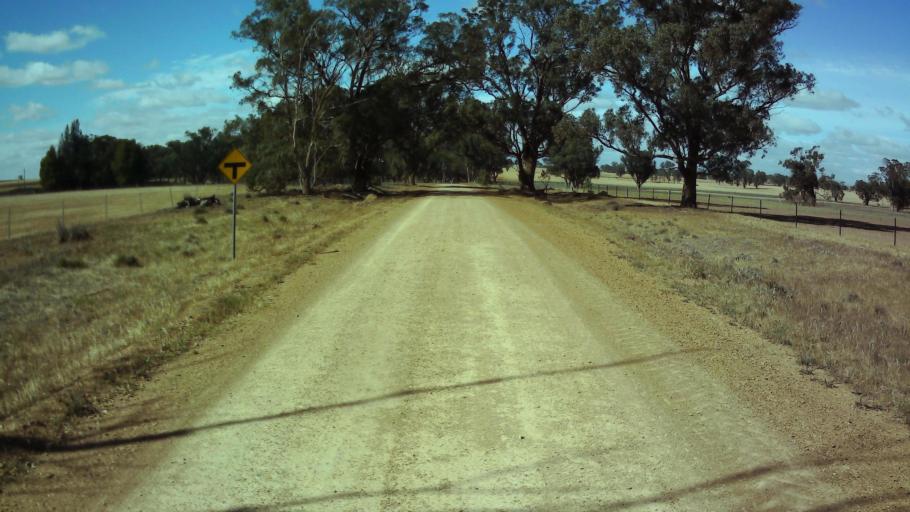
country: AU
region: New South Wales
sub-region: Weddin
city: Grenfell
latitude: -34.0636
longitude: 148.3115
